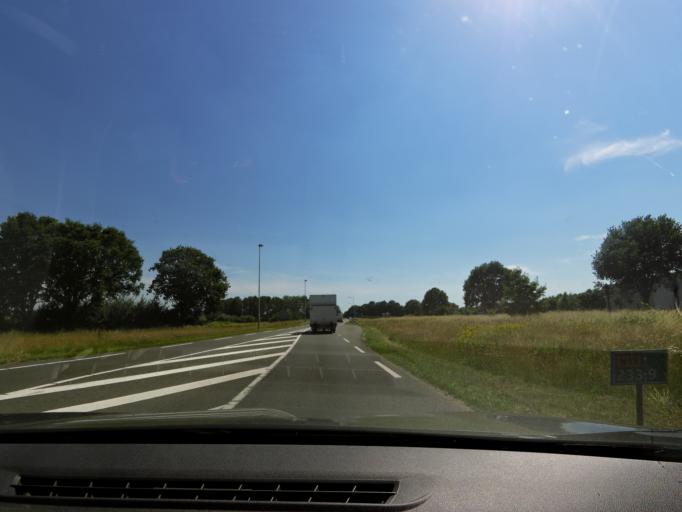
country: NL
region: Gelderland
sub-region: Berkelland
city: Eibergen
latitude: 52.0505
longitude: 6.6250
